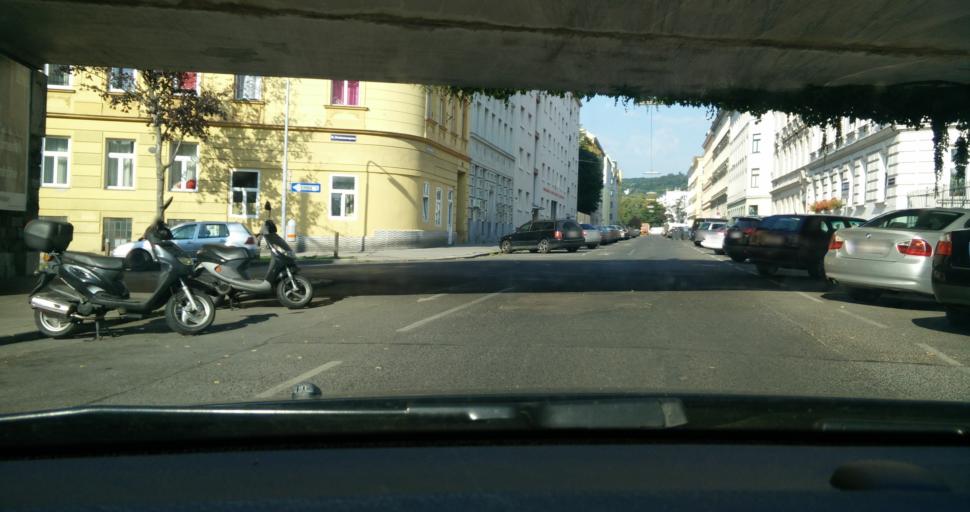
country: AT
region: Vienna
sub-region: Wien Stadt
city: Vienna
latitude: 48.2148
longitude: 16.3105
